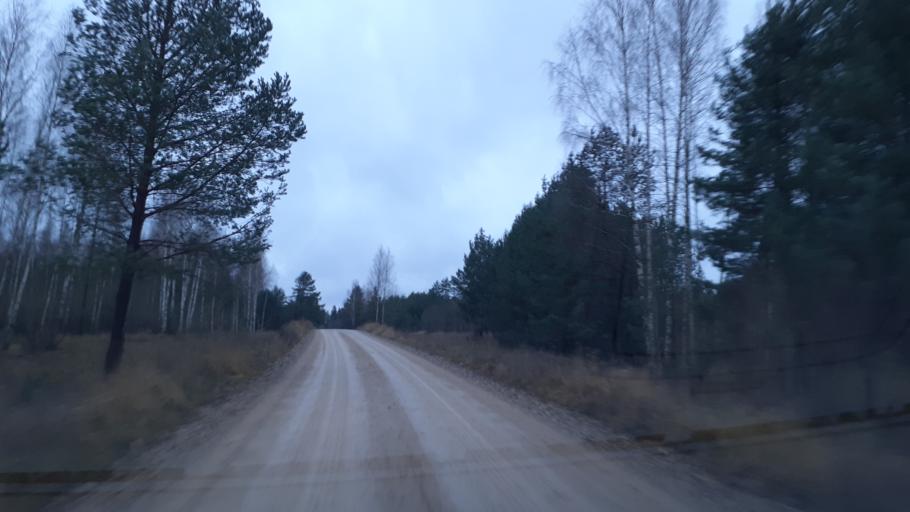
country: LV
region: Kuldigas Rajons
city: Kuldiga
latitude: 57.0533
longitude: 22.1213
